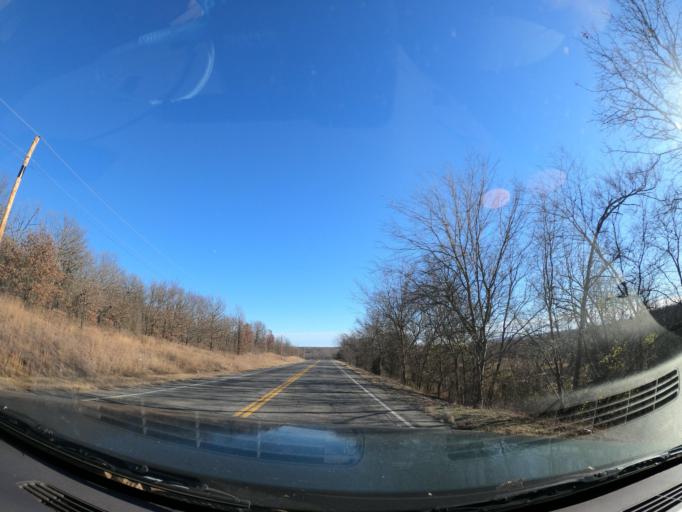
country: US
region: Oklahoma
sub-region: Pittsburg County
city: Longtown
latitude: 35.2177
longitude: -95.4254
